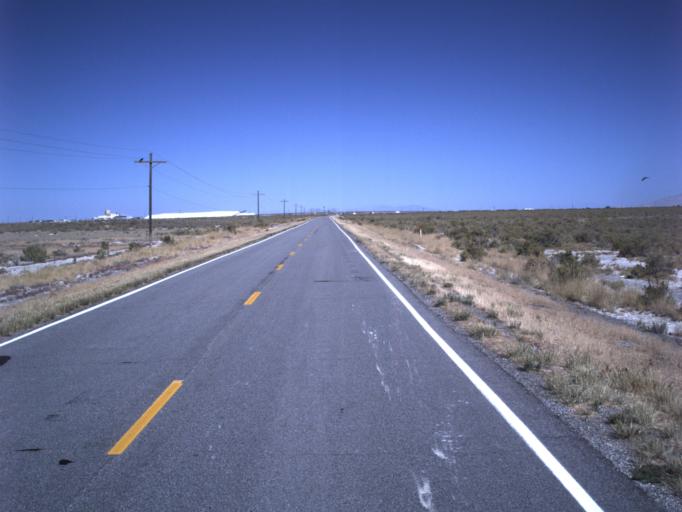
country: US
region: Utah
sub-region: Tooele County
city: Grantsville
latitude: 40.7274
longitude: -112.6583
